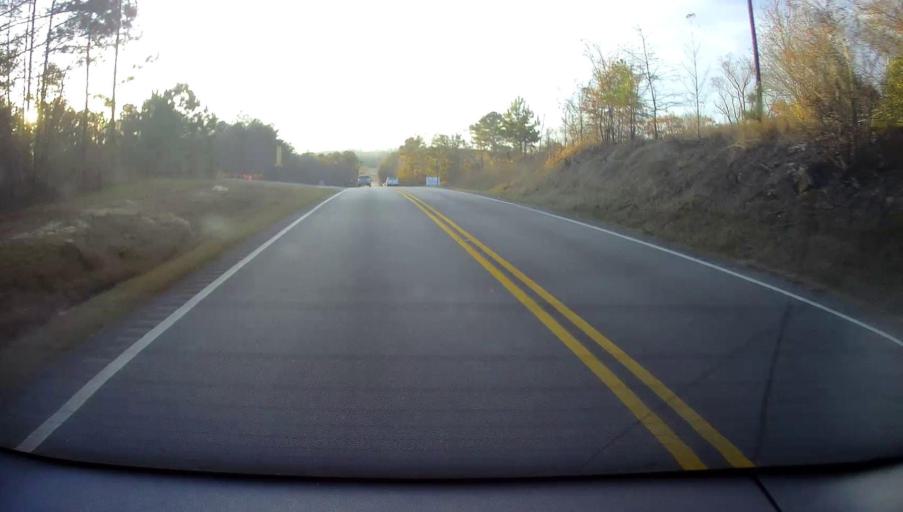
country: US
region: Alabama
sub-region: Saint Clair County
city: Steele
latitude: 34.0722
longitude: -86.3188
